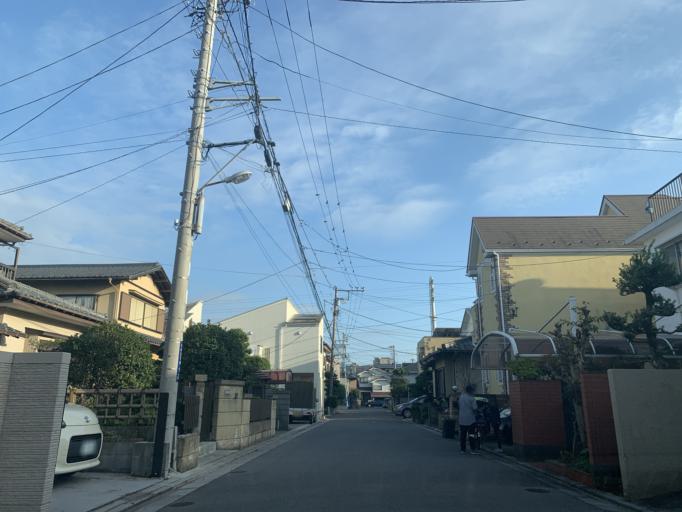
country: JP
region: Tokyo
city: Urayasu
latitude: 35.6402
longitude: 139.9072
